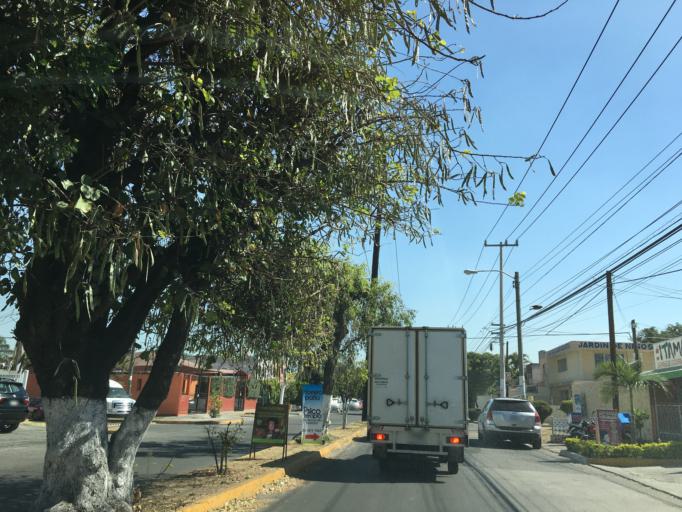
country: MX
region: Jalisco
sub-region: Tlajomulco de Zuniga
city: La Tijera
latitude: 20.6206
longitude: -103.4171
